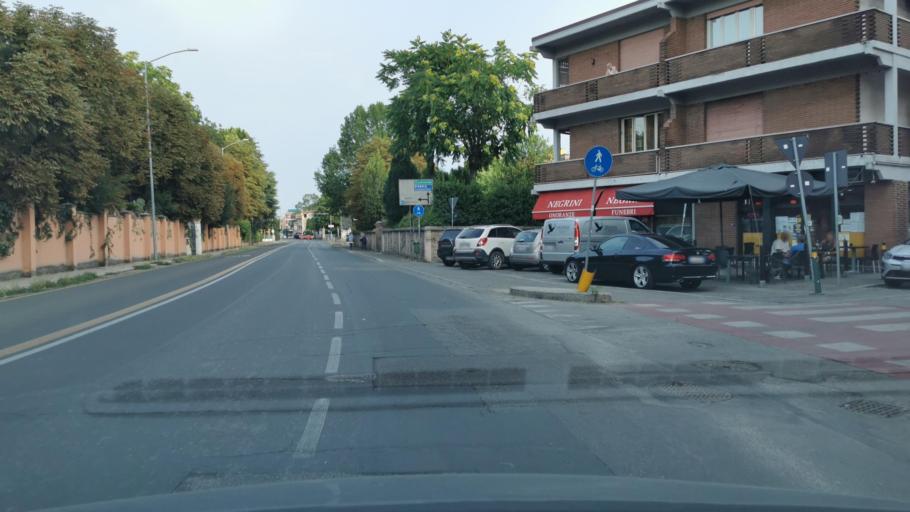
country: IT
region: Emilia-Romagna
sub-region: Provincia di Modena
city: Modena
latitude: 44.6351
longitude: 10.9349
